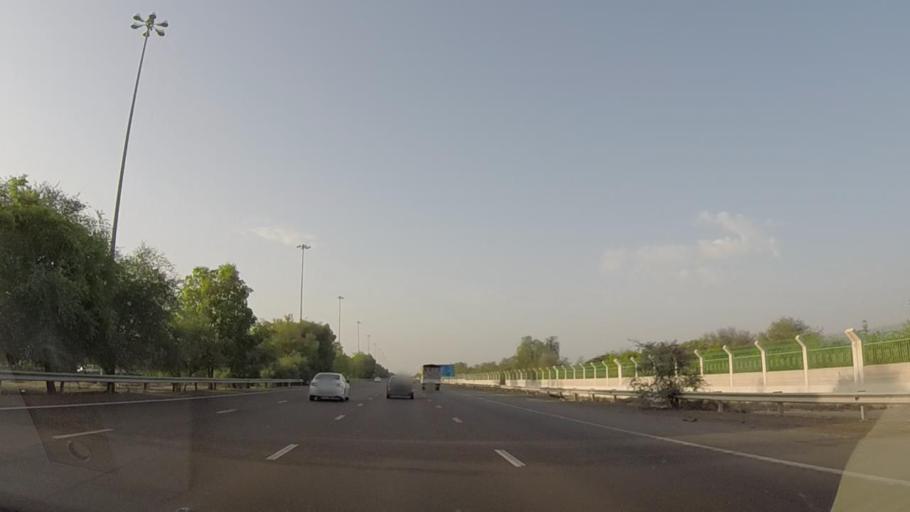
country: AE
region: Dubai
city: Dubai
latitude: 24.7794
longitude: 54.8535
